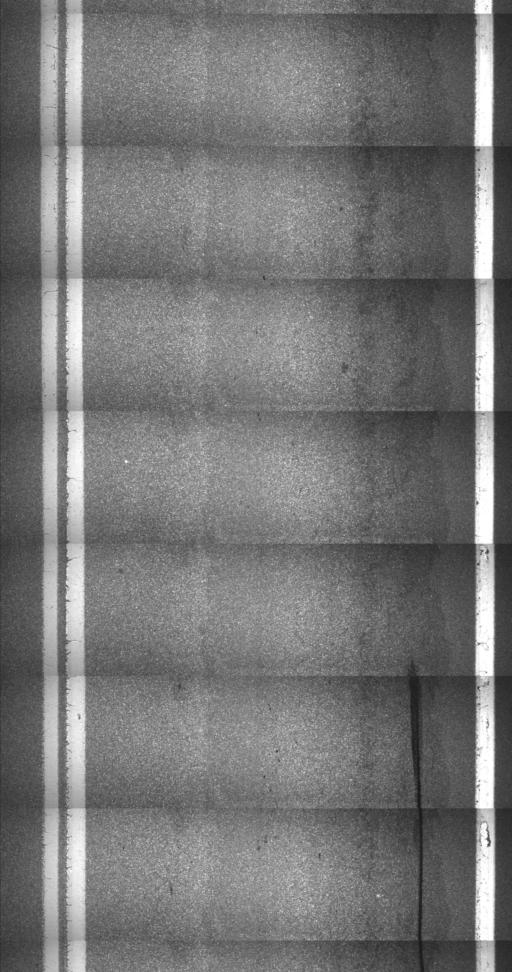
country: US
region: New York
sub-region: Washington County
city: Granville
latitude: 43.3278
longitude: -73.1727
